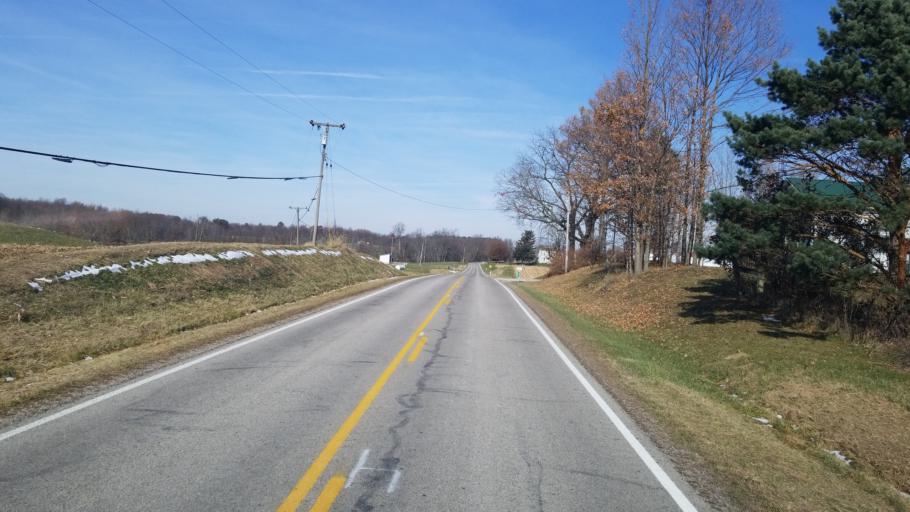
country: US
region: Ohio
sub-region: Huron County
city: Willard
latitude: 41.1113
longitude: -82.6861
